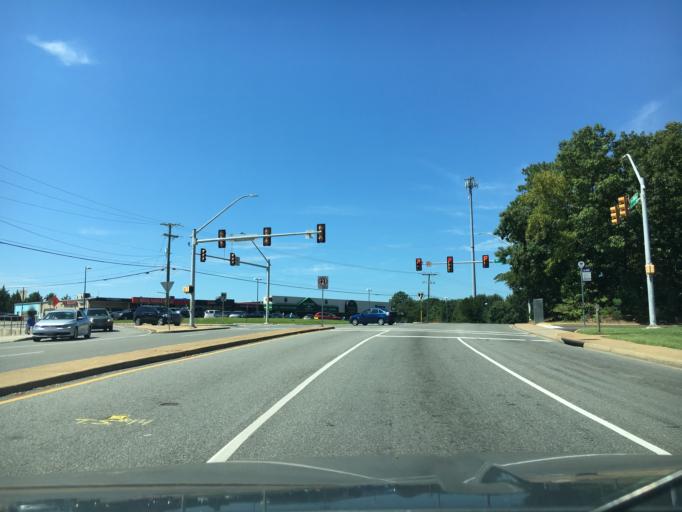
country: US
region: Virginia
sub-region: Henrico County
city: Tuckahoe
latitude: 37.6030
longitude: -77.5587
